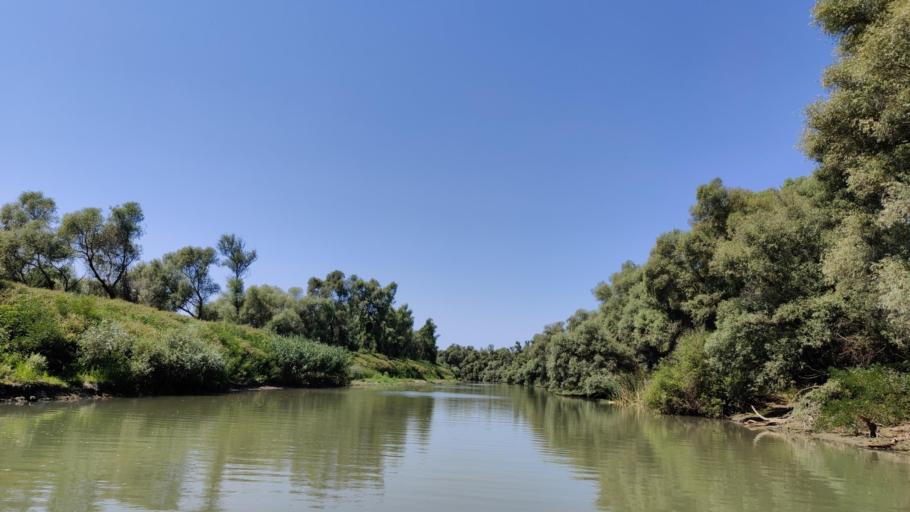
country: RO
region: Tulcea
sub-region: Comuna Pardina
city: Pardina
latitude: 45.2556
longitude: 28.9615
